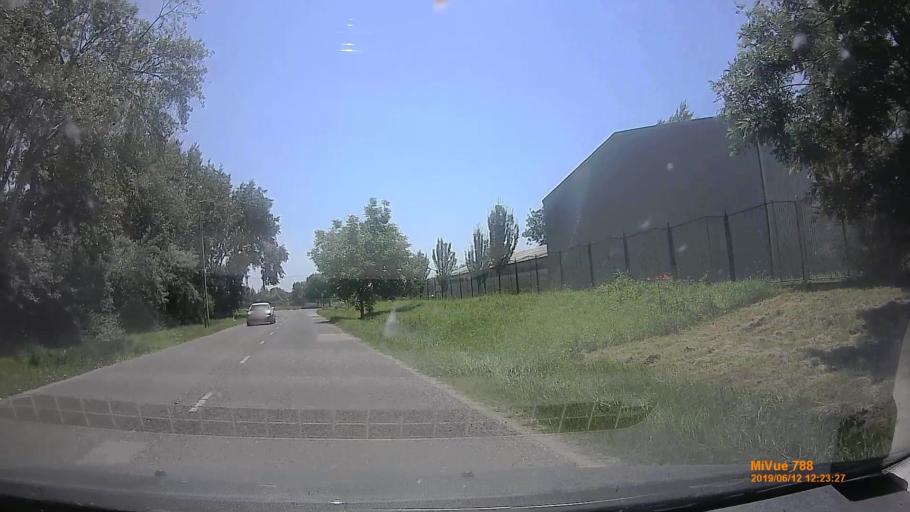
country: HU
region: Bacs-Kiskun
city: Kecskemet
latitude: 46.8922
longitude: 19.7011
